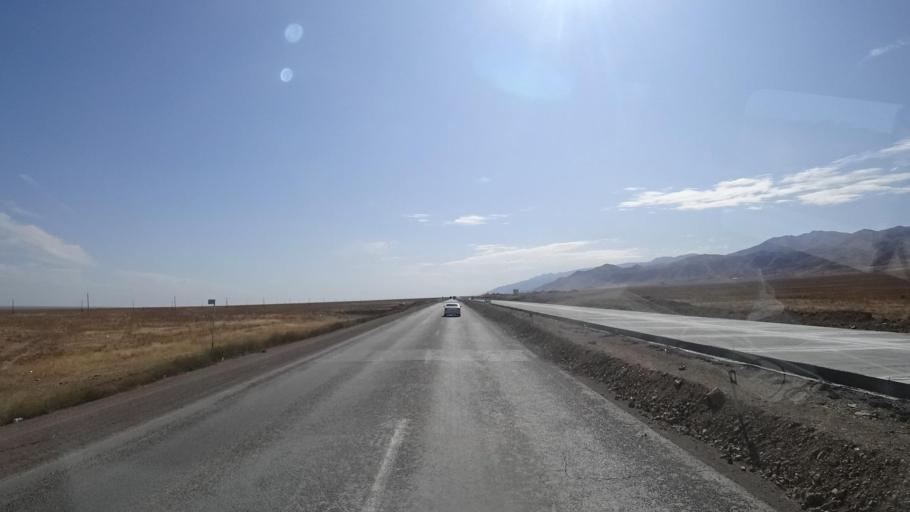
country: KG
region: Chuy
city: Ivanovka
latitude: 43.3977
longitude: 75.1219
